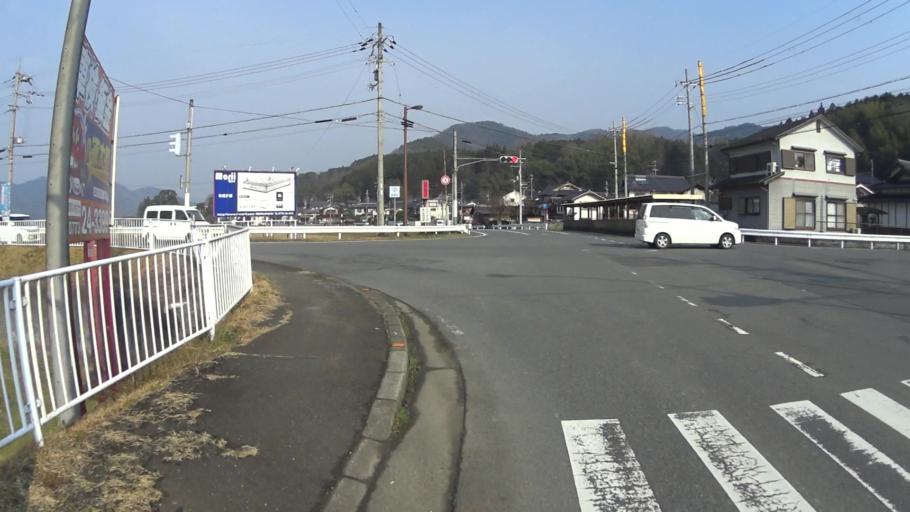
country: JP
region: Kyoto
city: Fukuchiyama
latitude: 35.3162
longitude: 135.1226
